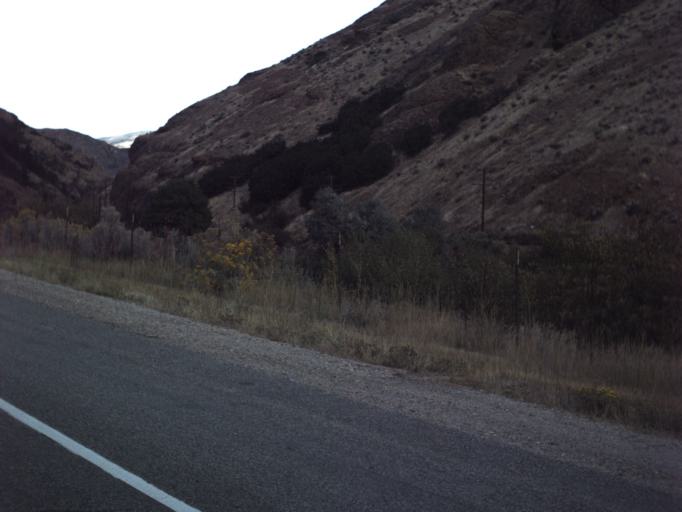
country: US
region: Utah
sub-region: Morgan County
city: Morgan
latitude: 41.0454
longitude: -111.5239
